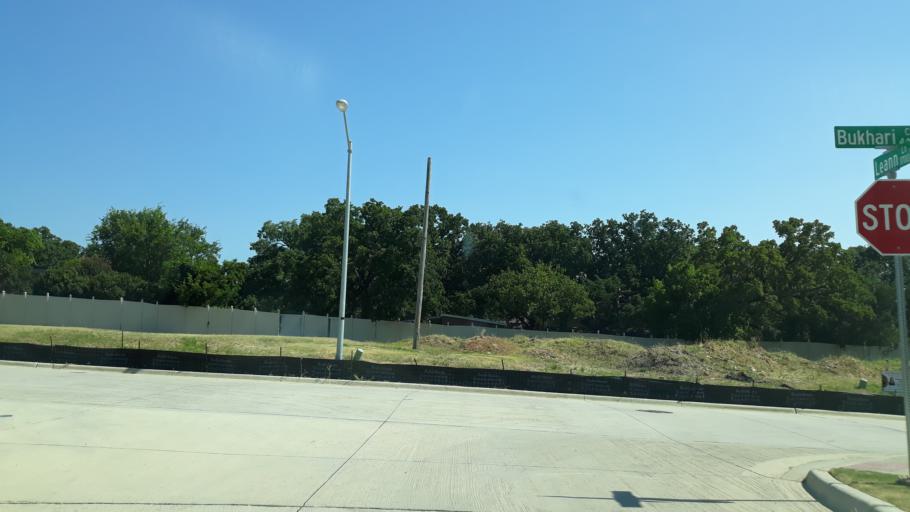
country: US
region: Texas
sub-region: Dallas County
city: Irving
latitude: 32.8306
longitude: -97.0126
